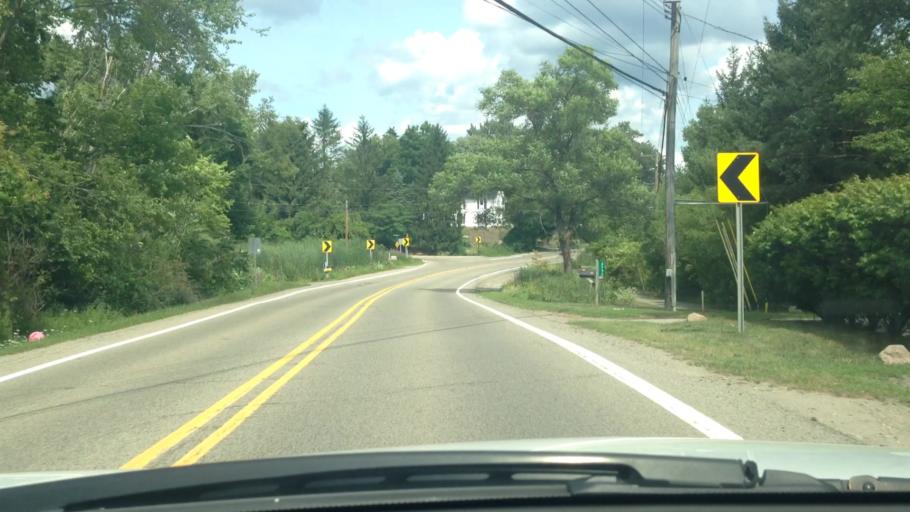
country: US
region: Michigan
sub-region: Oakland County
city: Clarkston
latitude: 42.7399
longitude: -83.4142
